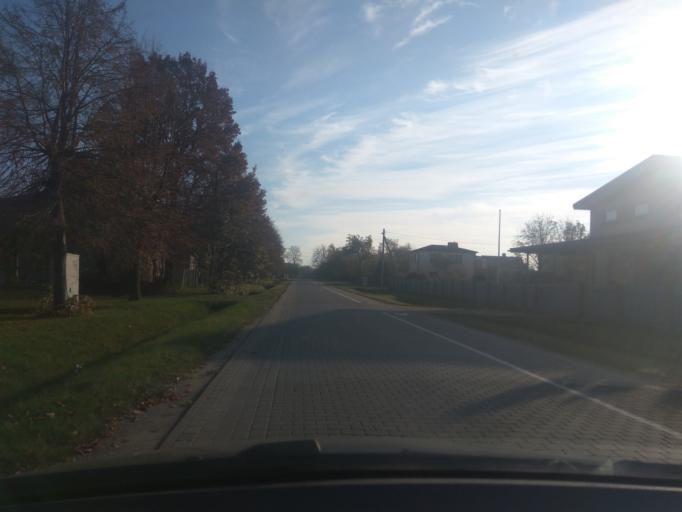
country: LV
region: Ventspils
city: Ventspils
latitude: 57.3814
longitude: 21.5775
